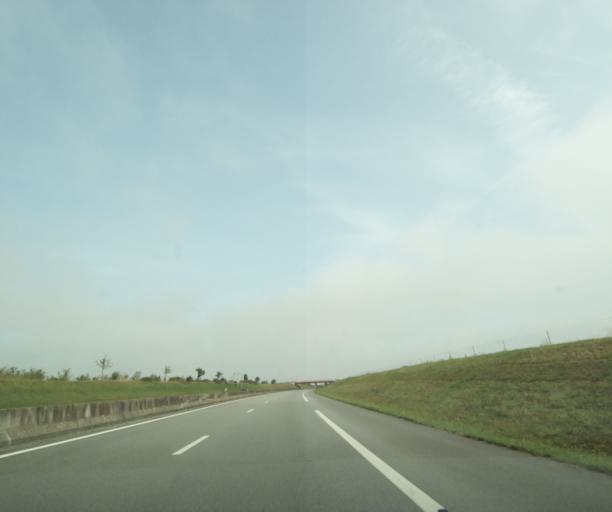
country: FR
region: Lower Normandy
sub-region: Departement de l'Orne
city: Sees
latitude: 48.6194
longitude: 0.1915
